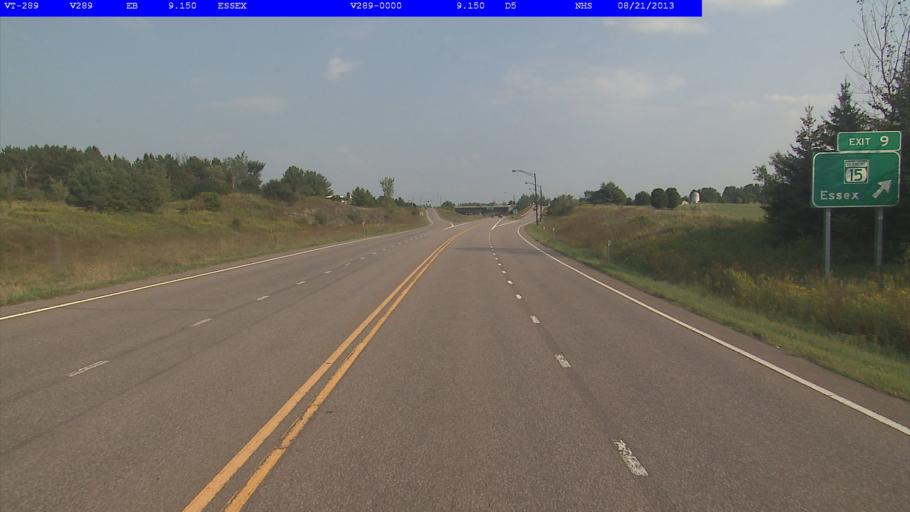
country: US
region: Vermont
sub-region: Chittenden County
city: Essex Junction
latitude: 44.5104
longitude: -73.0926
